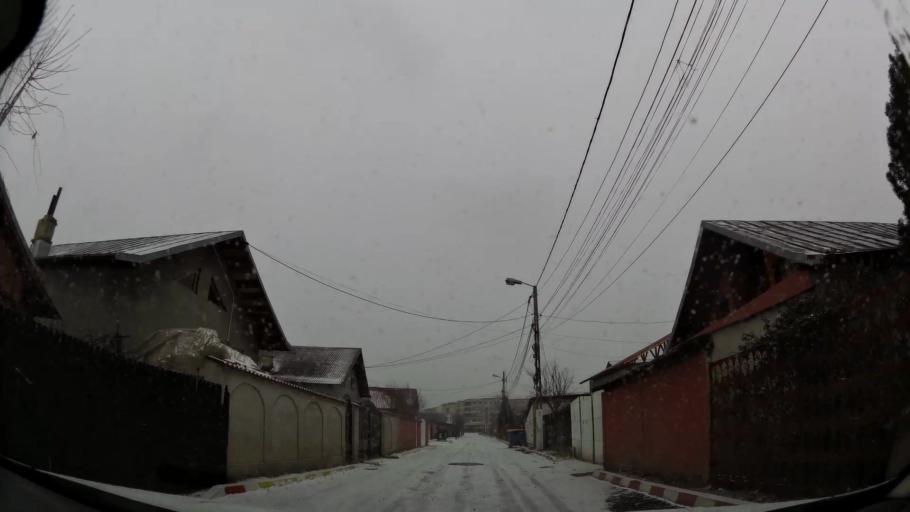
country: RO
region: Dambovita
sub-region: Comuna Ulmi
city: Ulmi
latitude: 44.9123
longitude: 25.4795
